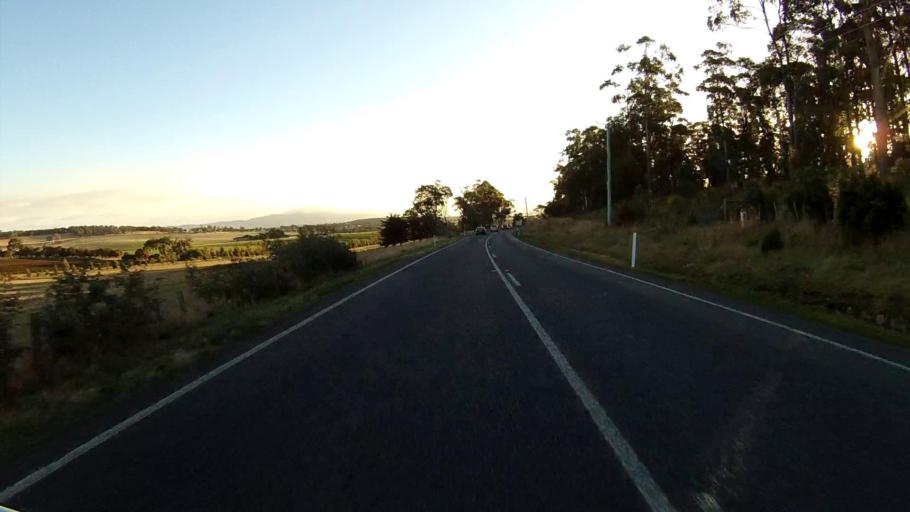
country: AU
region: Tasmania
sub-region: Sorell
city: Sorell
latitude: -42.8100
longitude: 147.6437
